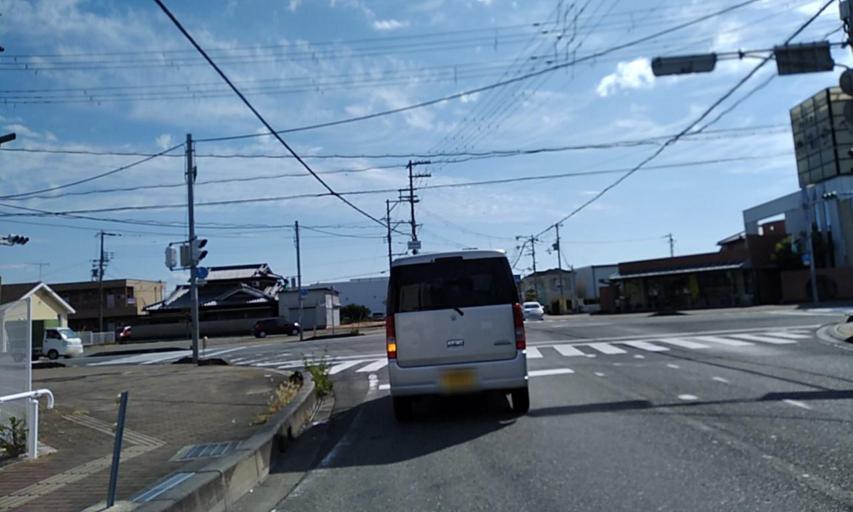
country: JP
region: Wakayama
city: Gobo
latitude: 33.9052
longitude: 135.1518
